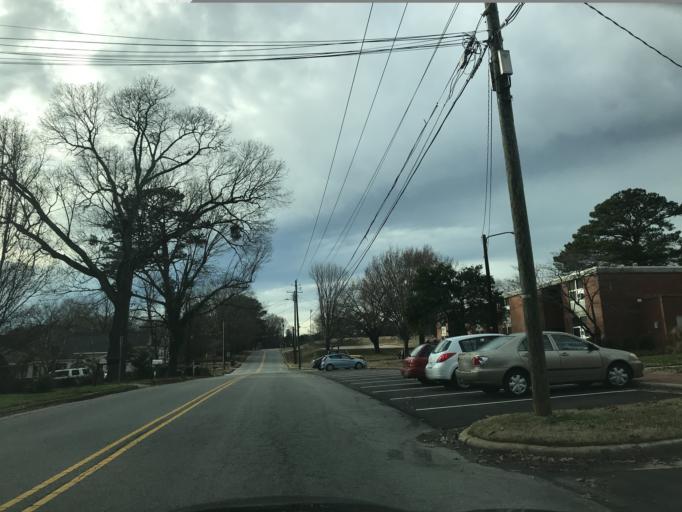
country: US
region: North Carolina
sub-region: Wake County
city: West Raleigh
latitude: 35.7870
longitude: -78.6901
